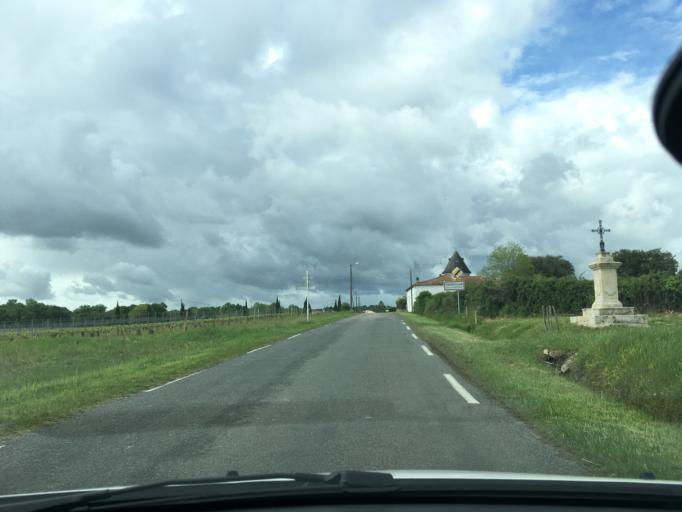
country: FR
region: Aquitaine
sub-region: Departement de la Gironde
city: Vertheuil
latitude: 45.3195
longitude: -0.8363
